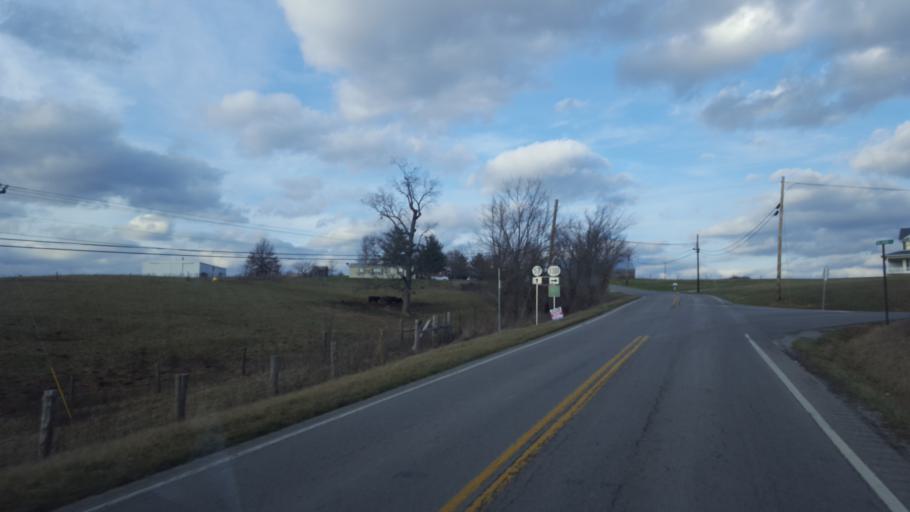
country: US
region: Kentucky
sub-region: Fleming County
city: Flemingsburg
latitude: 38.4428
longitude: -83.7015
